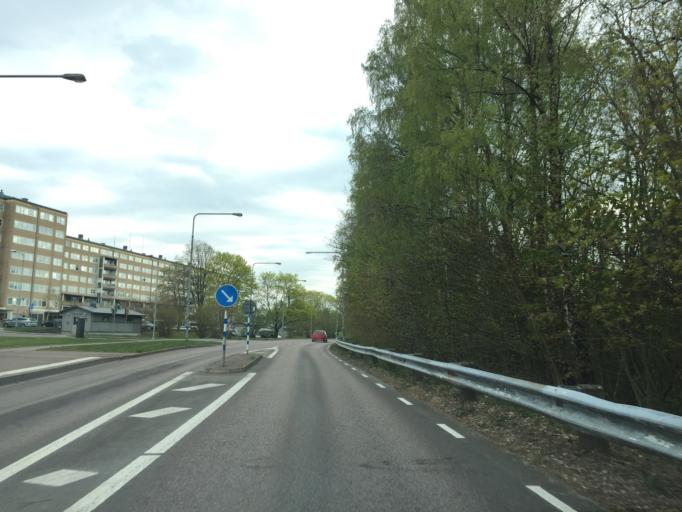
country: SE
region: Vaestra Goetaland
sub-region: Goteborg
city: Rannebergen
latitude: 57.8009
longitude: 12.0672
